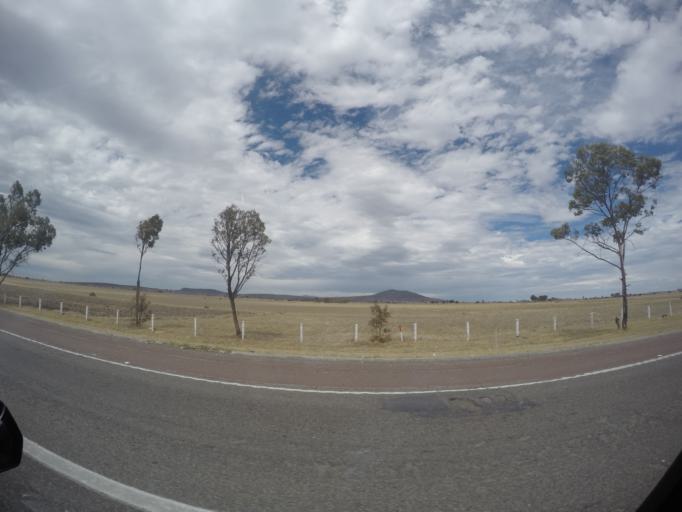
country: MX
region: Queretaro
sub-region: San Juan del Rio
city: El Cazadero
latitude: 20.2709
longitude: -99.8756
